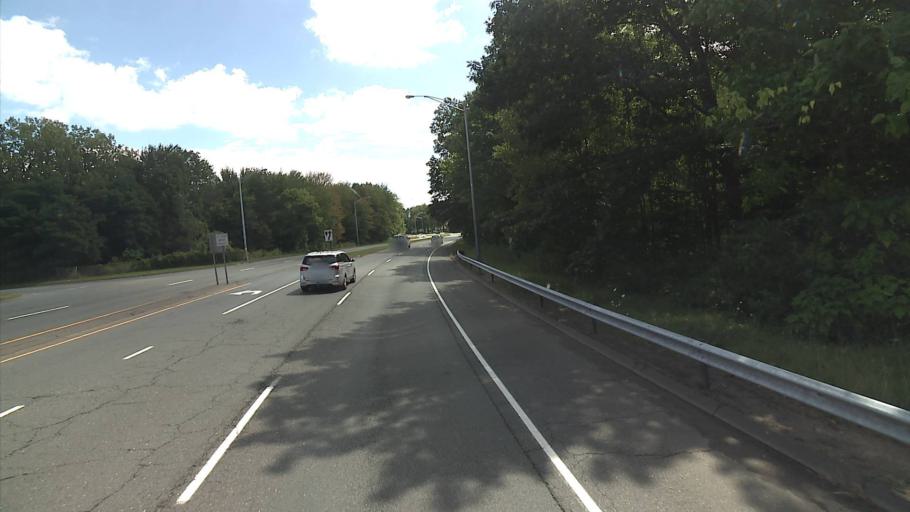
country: US
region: Connecticut
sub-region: Hartford County
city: Blue Hills
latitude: 41.8175
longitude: -72.7012
